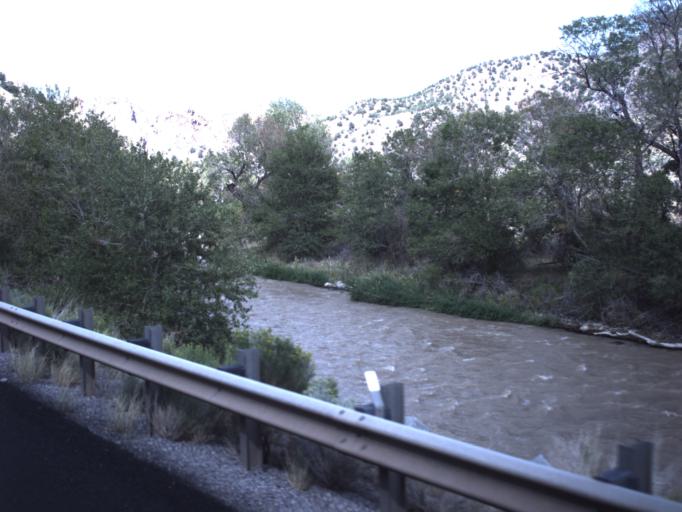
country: US
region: Utah
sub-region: Sevier County
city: Monroe
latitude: 38.5620
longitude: -112.2729
